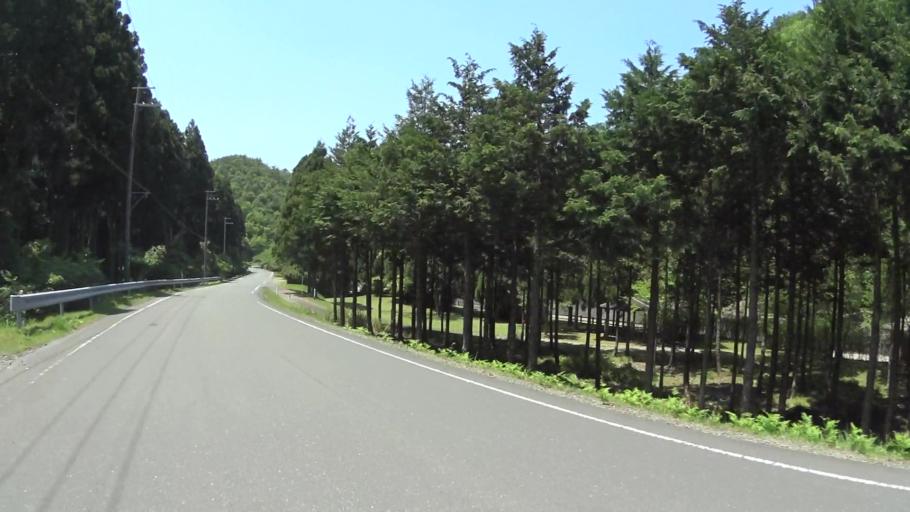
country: JP
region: Kyoto
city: Kameoka
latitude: 35.0848
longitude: 135.5743
